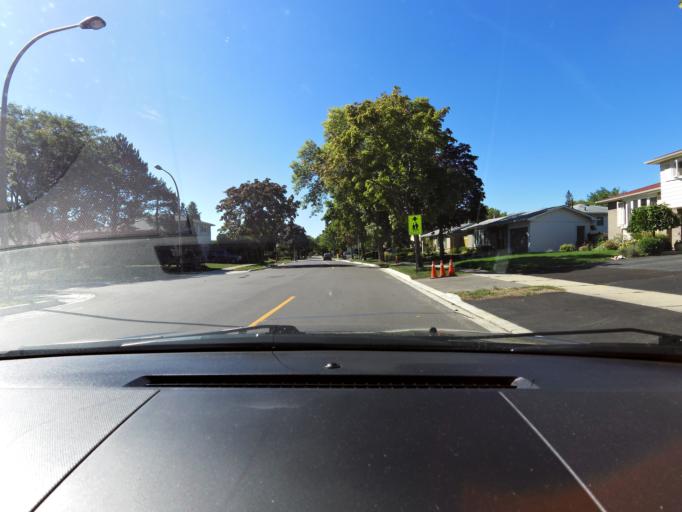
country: CA
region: Ontario
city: Burlington
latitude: 43.3687
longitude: -79.8133
